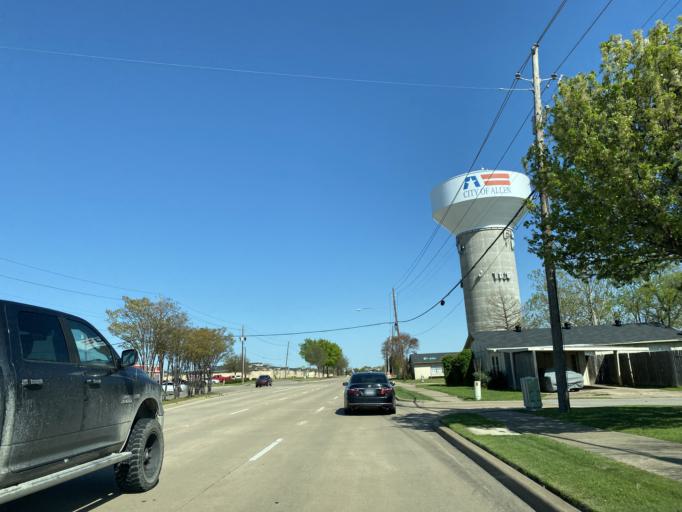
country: US
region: Texas
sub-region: Collin County
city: Allen
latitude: 33.1003
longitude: -96.6506
